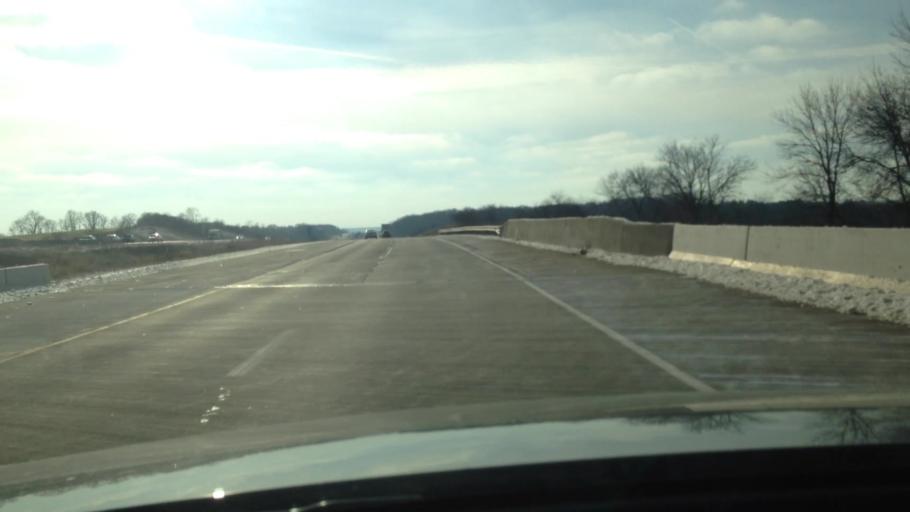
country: US
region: Wisconsin
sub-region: Waukesha County
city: Big Bend
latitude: 42.8984
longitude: -88.2582
